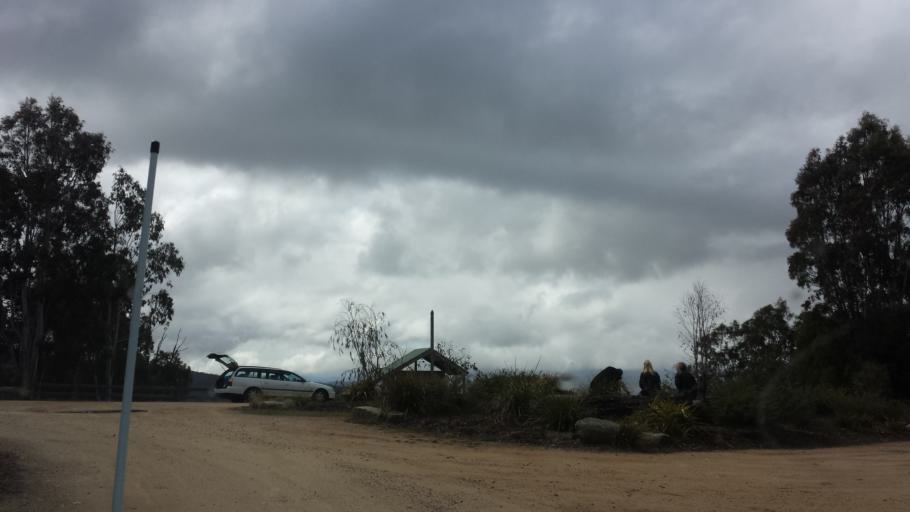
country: AU
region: Victoria
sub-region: Alpine
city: Mount Beauty
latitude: -37.1270
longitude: 147.5342
